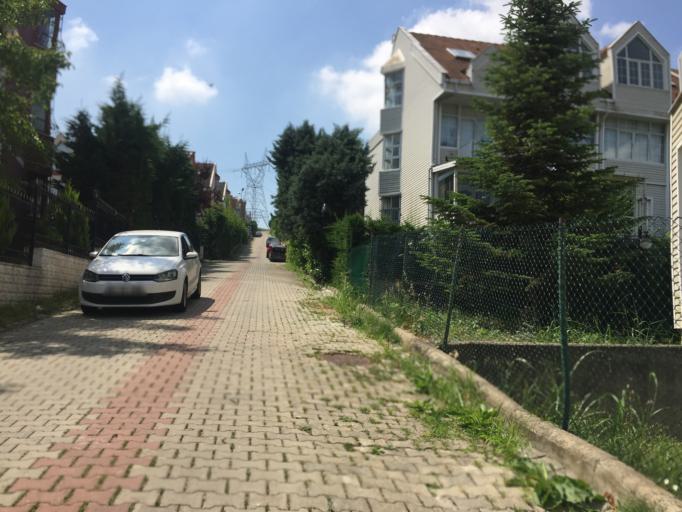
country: TR
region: Istanbul
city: Esenyurt
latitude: 41.0812
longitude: 28.6686
